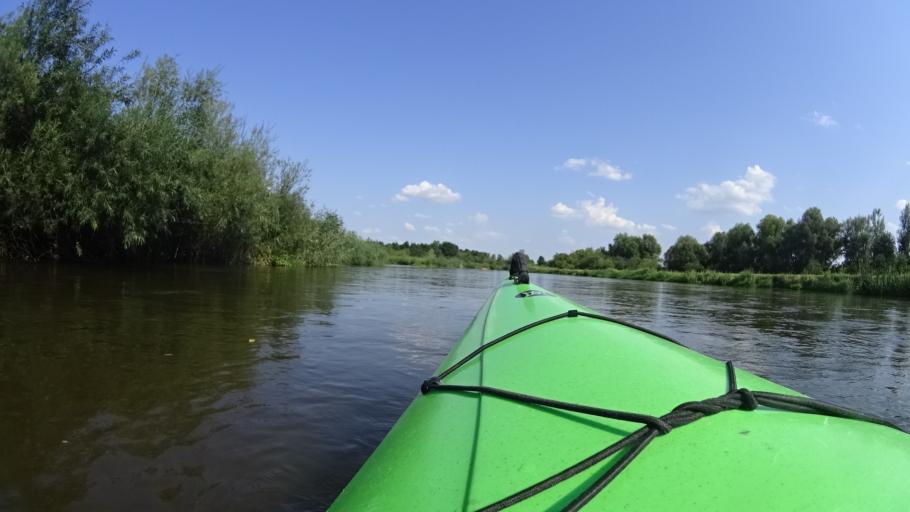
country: PL
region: Masovian Voivodeship
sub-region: Powiat bialobrzeski
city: Bialobrzegi
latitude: 51.6644
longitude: 20.8940
